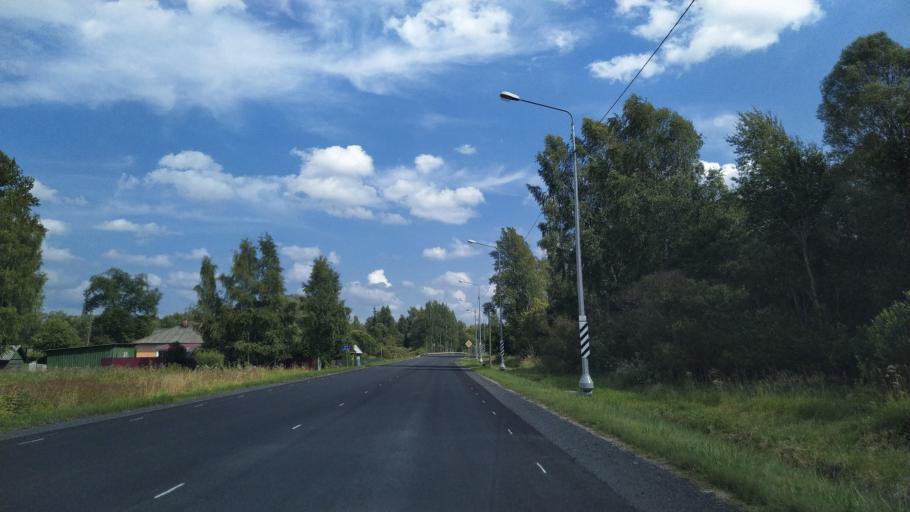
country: RU
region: Pskov
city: Porkhov
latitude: 57.7275
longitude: 29.1611
